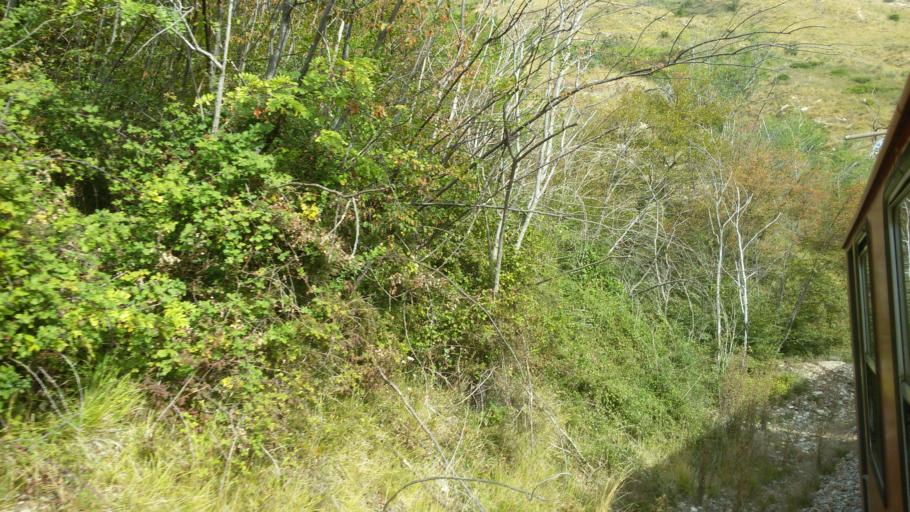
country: IT
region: Liguria
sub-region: Provincia di Genova
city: Manesseno
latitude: 44.4476
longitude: 8.9436
